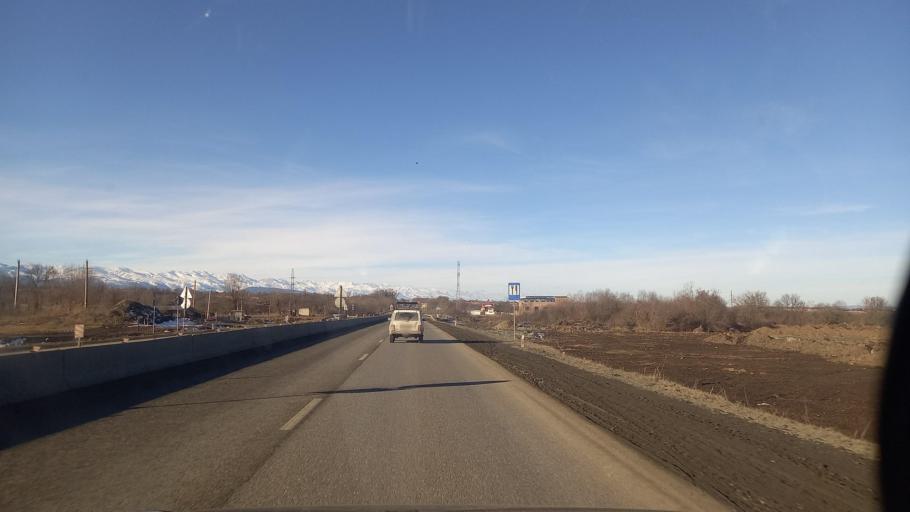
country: RU
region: North Ossetia
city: Gizel'
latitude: 43.0279
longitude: 44.6035
